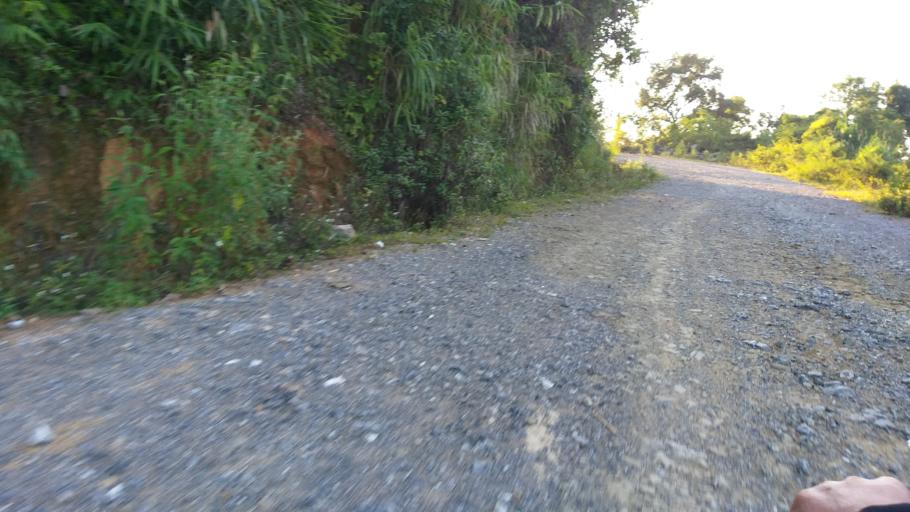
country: LA
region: Phongsali
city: Khoa
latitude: 21.2166
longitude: 102.5923
